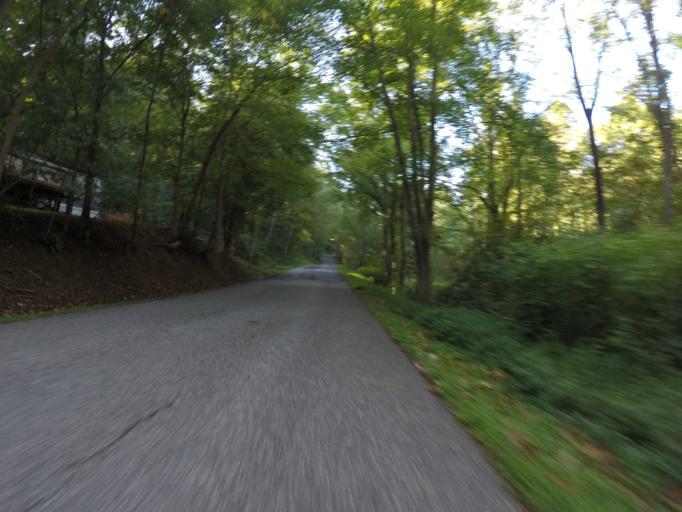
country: US
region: Kentucky
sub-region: Boyd County
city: Ashland
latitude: 38.5297
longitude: -82.5336
